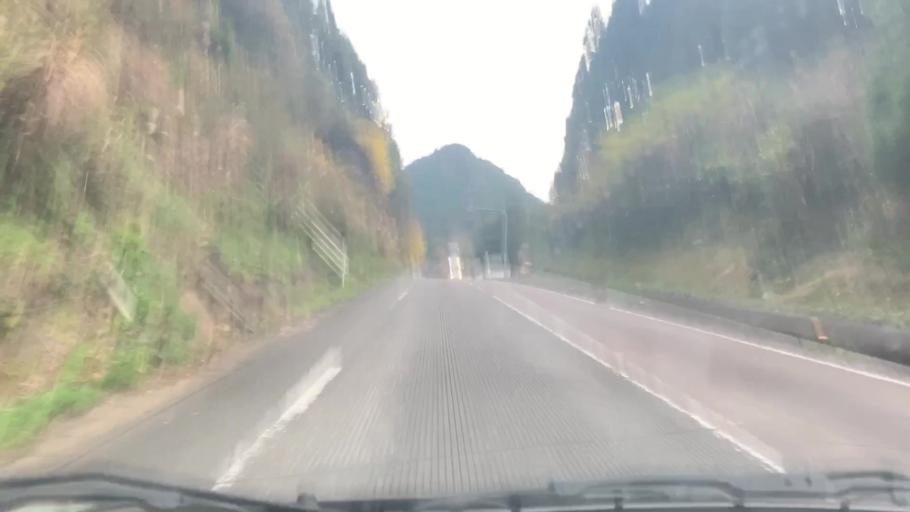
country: JP
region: Saga Prefecture
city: Kashima
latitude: 33.0544
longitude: 130.0720
